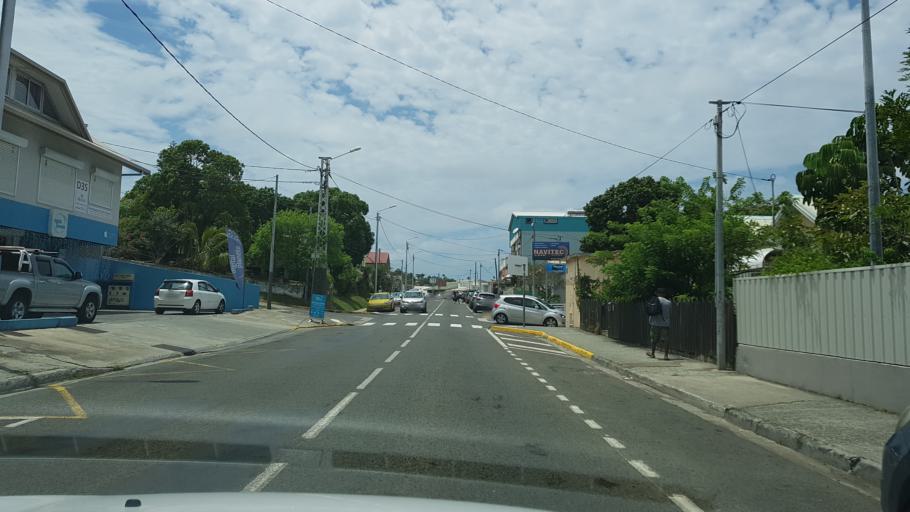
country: NC
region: South Province
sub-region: Noumea
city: Noumea
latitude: -22.2835
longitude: 166.4535
